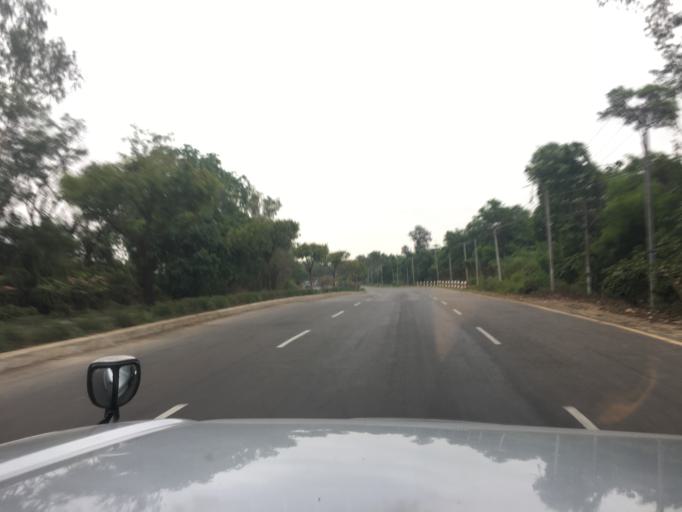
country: MM
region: Bago
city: Bago
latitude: 17.2188
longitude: 96.4338
